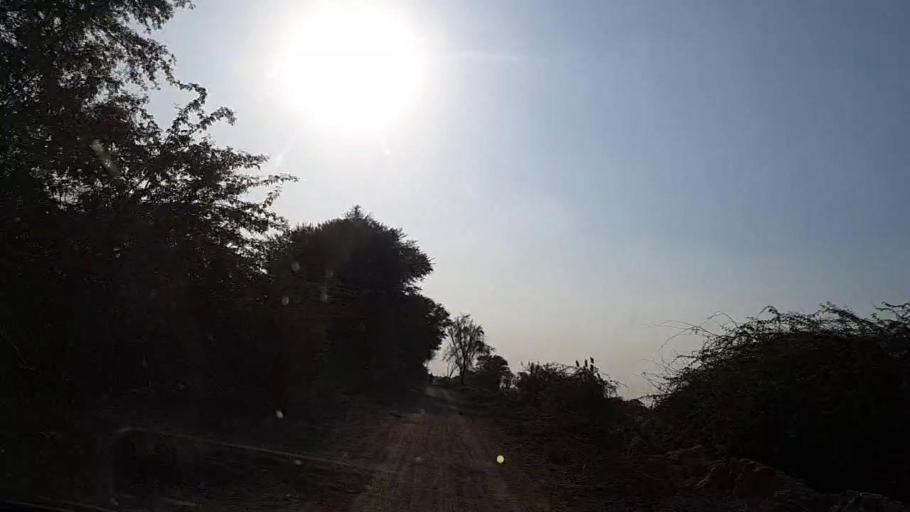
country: PK
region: Sindh
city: Sakrand
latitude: 26.0935
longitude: 68.2125
